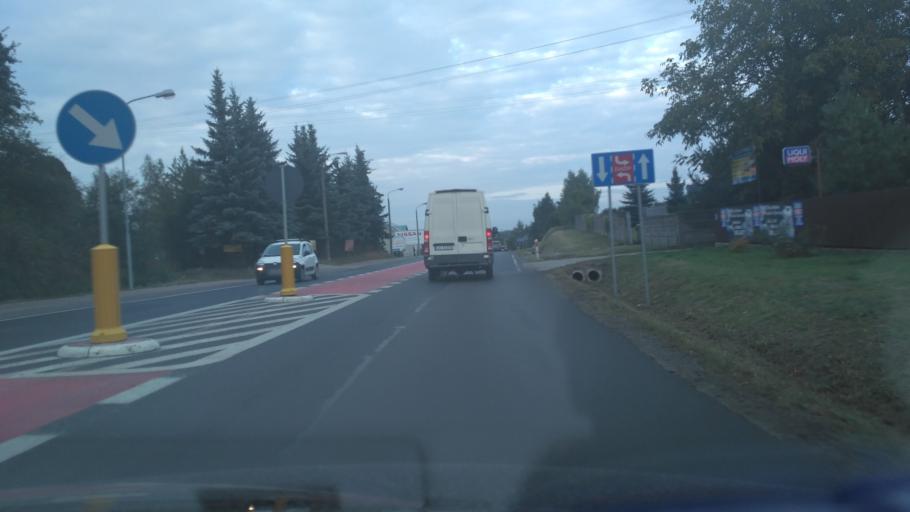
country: PL
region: Lublin Voivodeship
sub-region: Powiat lubelski
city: Jakubowice Murowane
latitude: 51.2716
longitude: 22.6413
